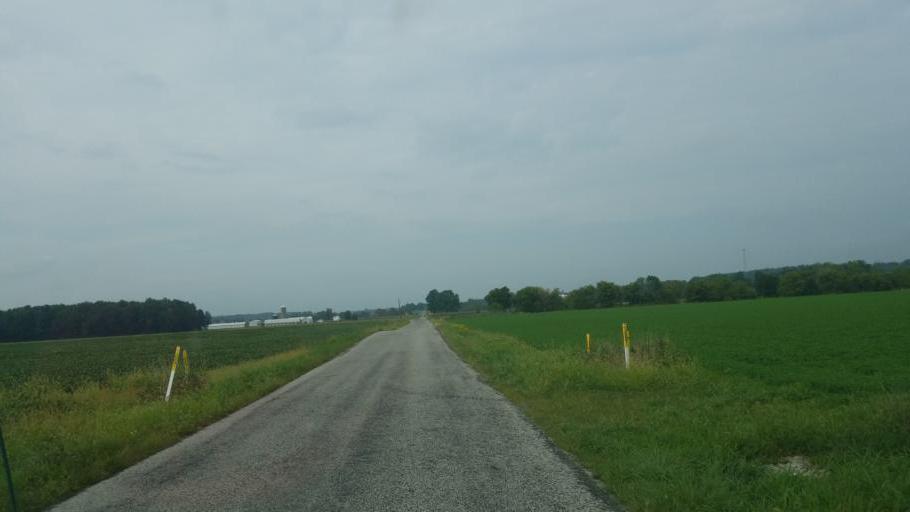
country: US
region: Ohio
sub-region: Wayne County
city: Rittman
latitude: 40.9529
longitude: -81.8121
